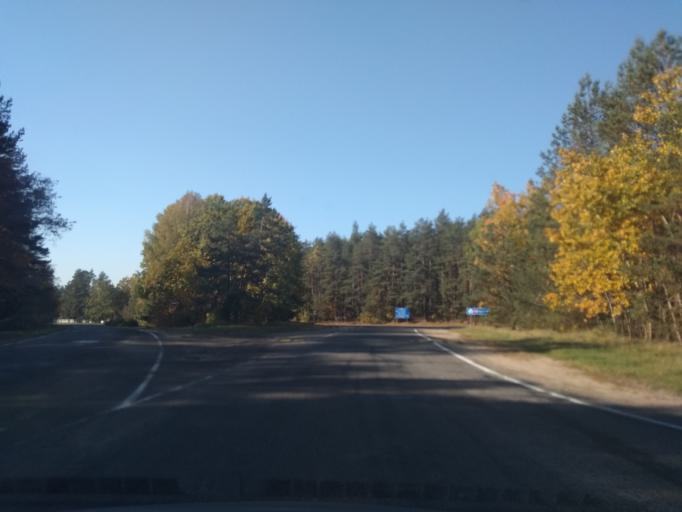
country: BY
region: Brest
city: Ivatsevichy
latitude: 52.8556
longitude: 25.6392
